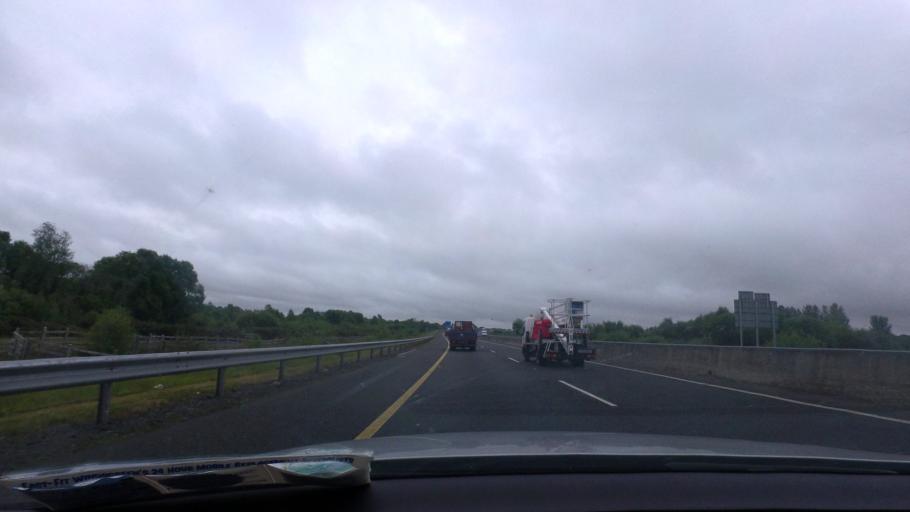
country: IE
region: Munster
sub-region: County Limerick
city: Castleconnell
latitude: 52.6895
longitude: -8.4988
